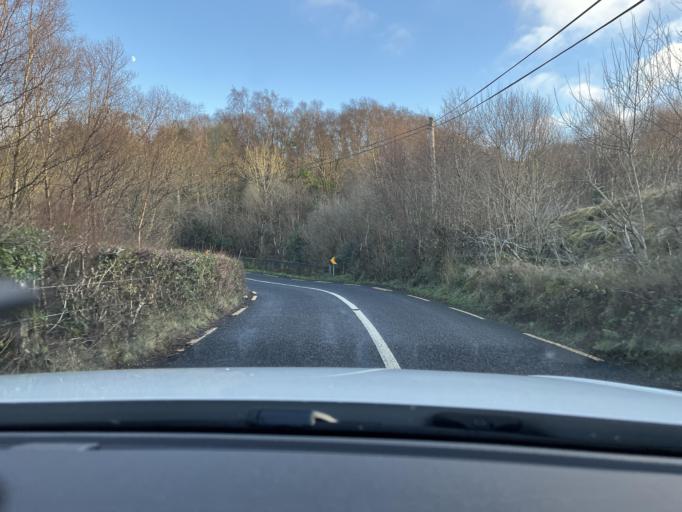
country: IE
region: Connaught
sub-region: County Leitrim
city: Manorhamilton
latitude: 54.2001
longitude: -7.9547
